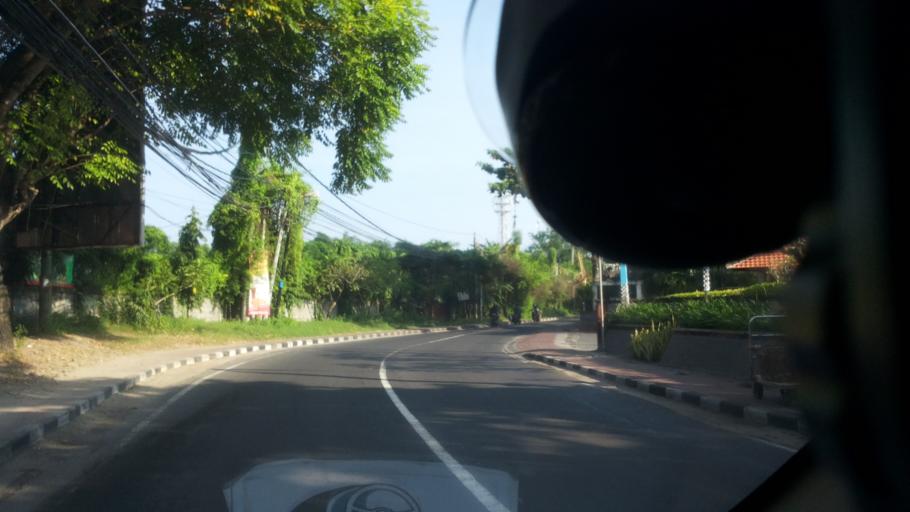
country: ID
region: Bali
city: Bualu
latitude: -8.7872
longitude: 115.2259
